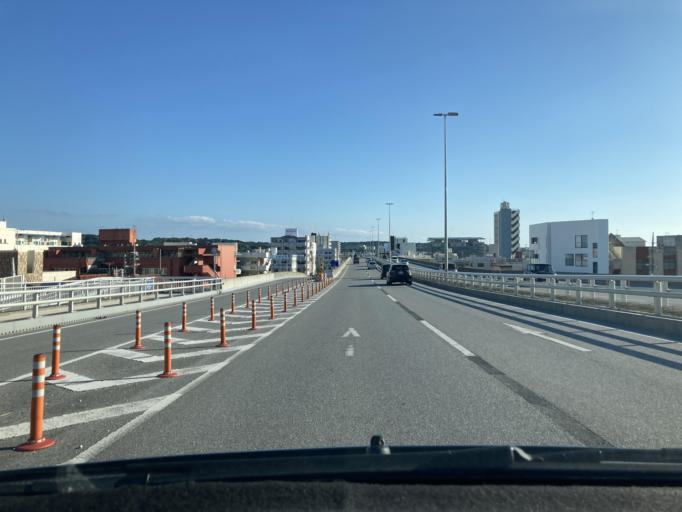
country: JP
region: Okinawa
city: Itoman
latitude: 26.1301
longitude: 127.6653
